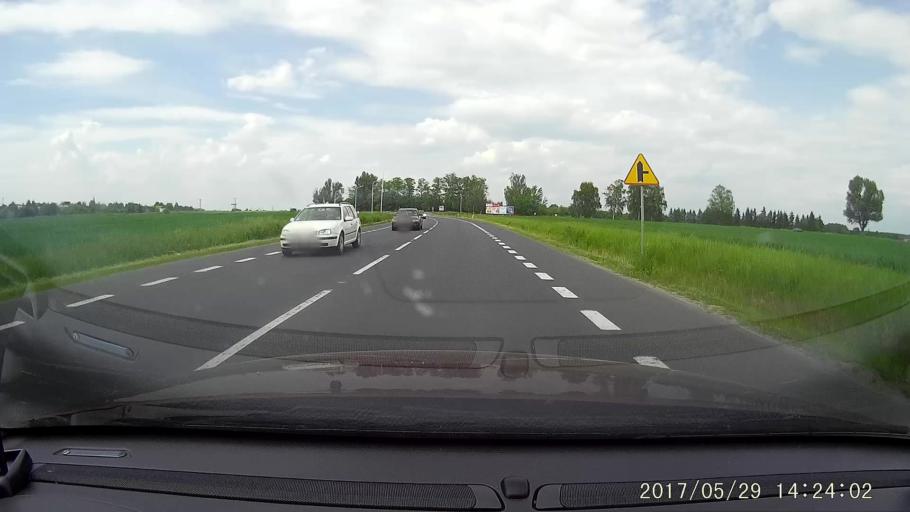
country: PL
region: Lower Silesian Voivodeship
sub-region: Powiat zgorzelecki
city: Lagow
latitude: 51.1432
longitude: 15.0340
